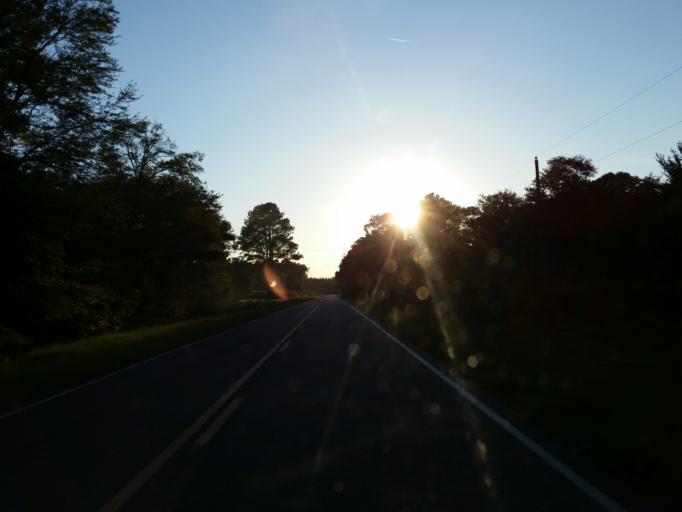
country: US
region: Georgia
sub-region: Berrien County
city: Nashville
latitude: 31.1787
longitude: -83.1300
